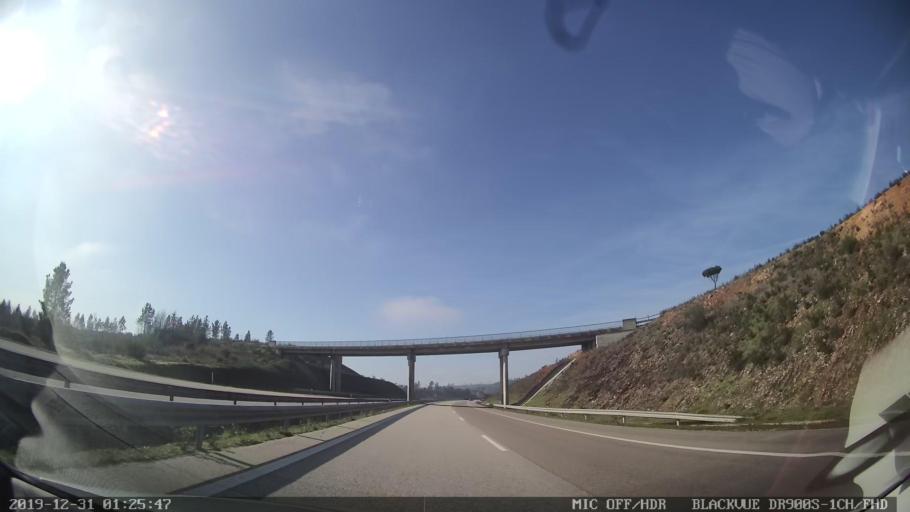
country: PT
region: Santarem
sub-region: Macao
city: Macao
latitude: 39.4926
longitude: -8.0577
